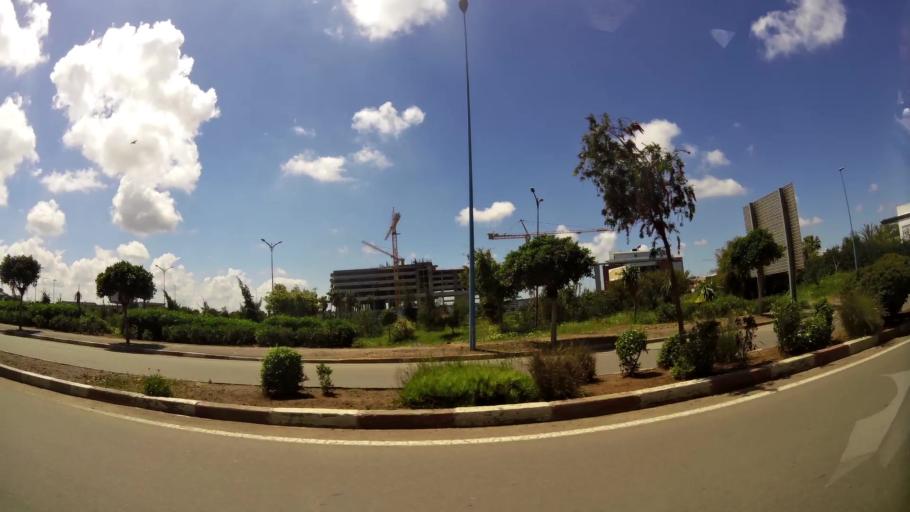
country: MA
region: Grand Casablanca
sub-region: Casablanca
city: Casablanca
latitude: 33.5215
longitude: -7.6319
